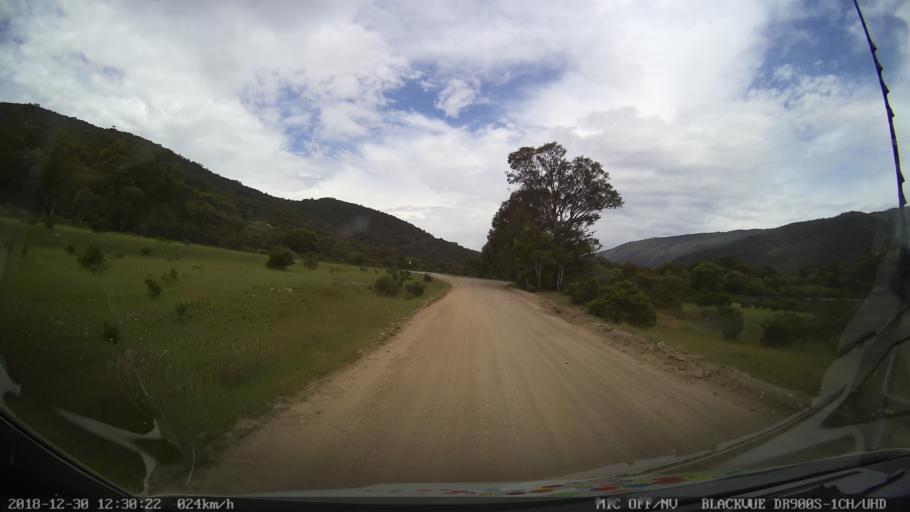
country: AU
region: New South Wales
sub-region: Snowy River
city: Jindabyne
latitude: -36.3240
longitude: 148.4747
